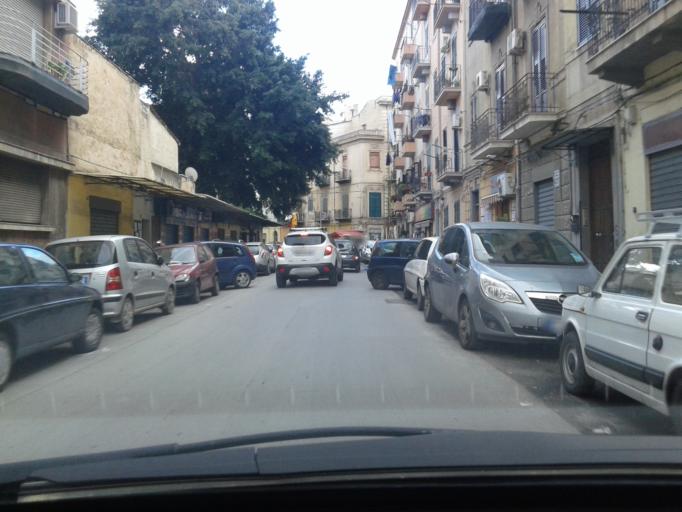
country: IT
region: Sicily
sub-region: Palermo
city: Palermo
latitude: 38.1150
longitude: 13.3455
